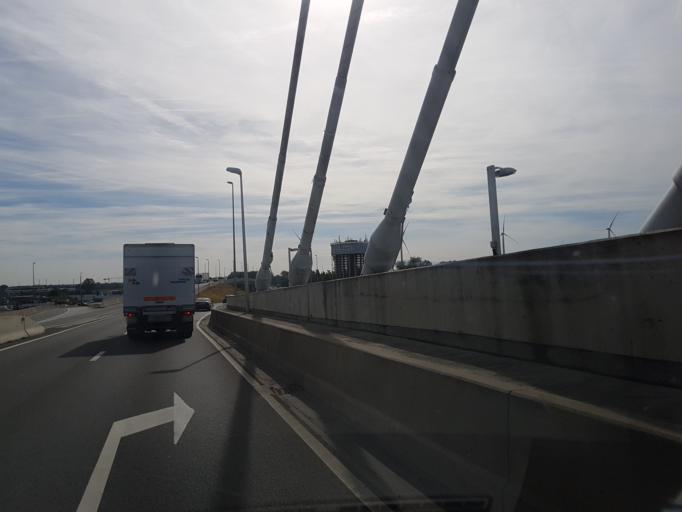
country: BE
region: Flanders
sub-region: Provincie Antwerpen
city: Westerlo
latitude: 51.1361
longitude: 4.9399
